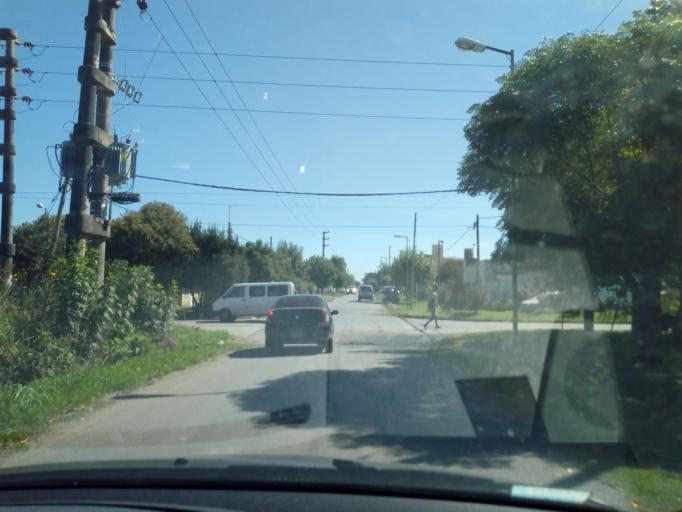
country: AR
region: Buenos Aires
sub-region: Partido de La Plata
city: La Plata
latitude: -35.0009
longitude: -58.0477
